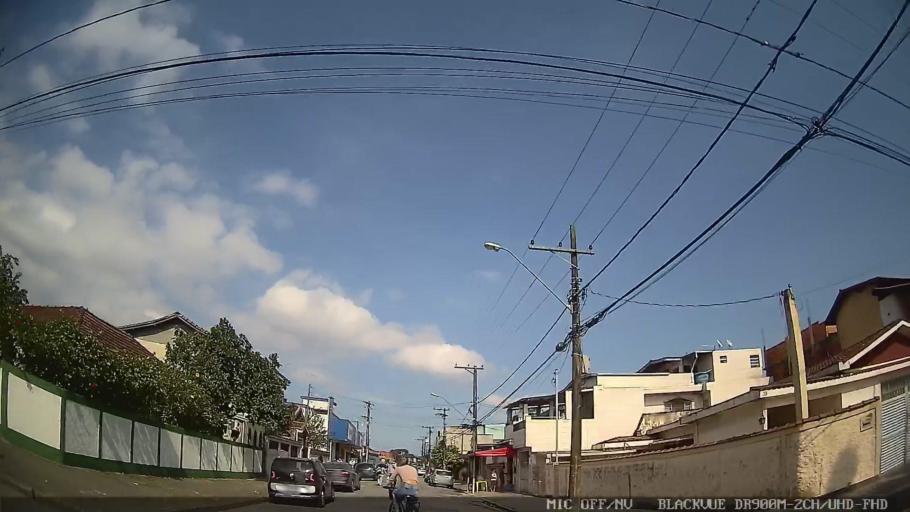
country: BR
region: Sao Paulo
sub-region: Santos
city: Santos
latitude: -23.9439
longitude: -46.3039
